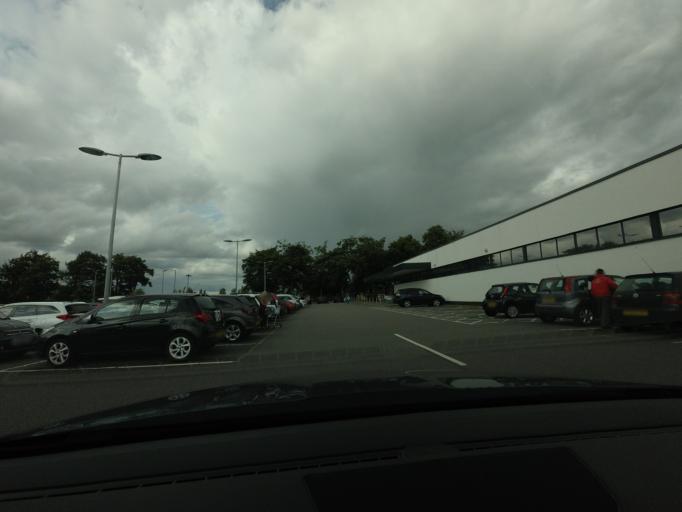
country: GB
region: Scotland
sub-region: Highland
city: Inverness
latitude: 57.4686
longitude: -4.1893
